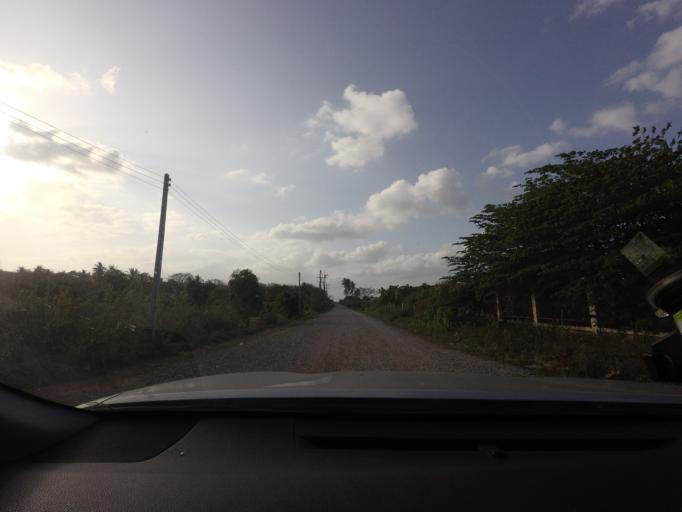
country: TH
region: Pattani
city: Mae Lan
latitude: 6.6146
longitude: 101.2576
